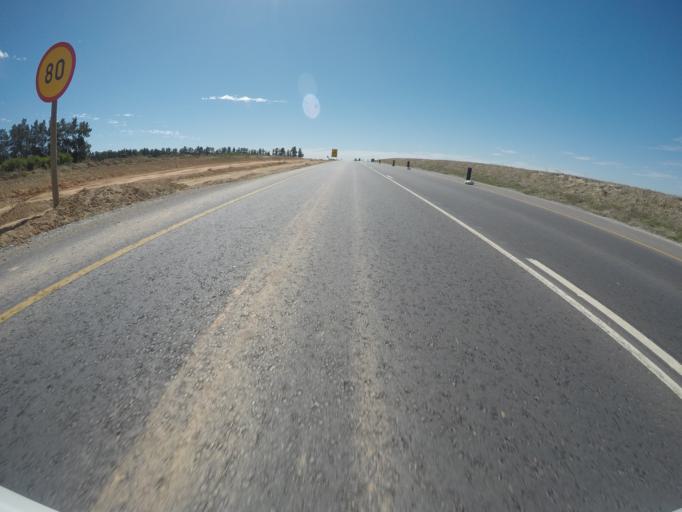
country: ZA
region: Western Cape
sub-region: West Coast District Municipality
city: Malmesbury
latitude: -33.5026
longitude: 18.6629
